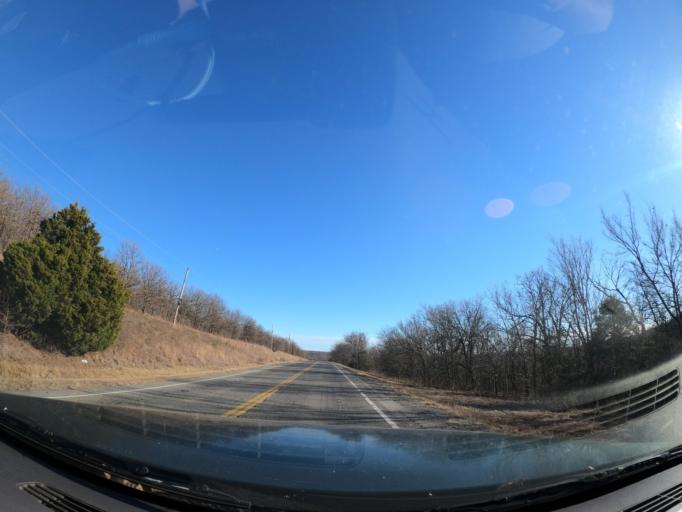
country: US
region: Oklahoma
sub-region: Pittsburg County
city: Longtown
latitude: 35.2185
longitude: -95.4265
